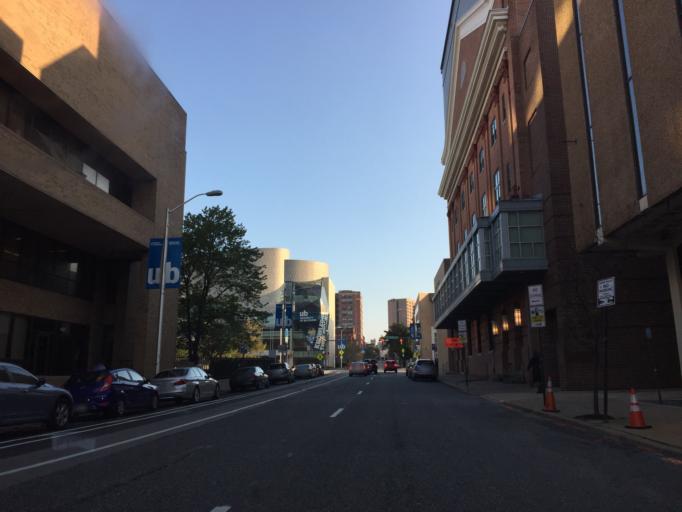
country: US
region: Maryland
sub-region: City of Baltimore
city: Baltimore
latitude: 39.3064
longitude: -76.6177
